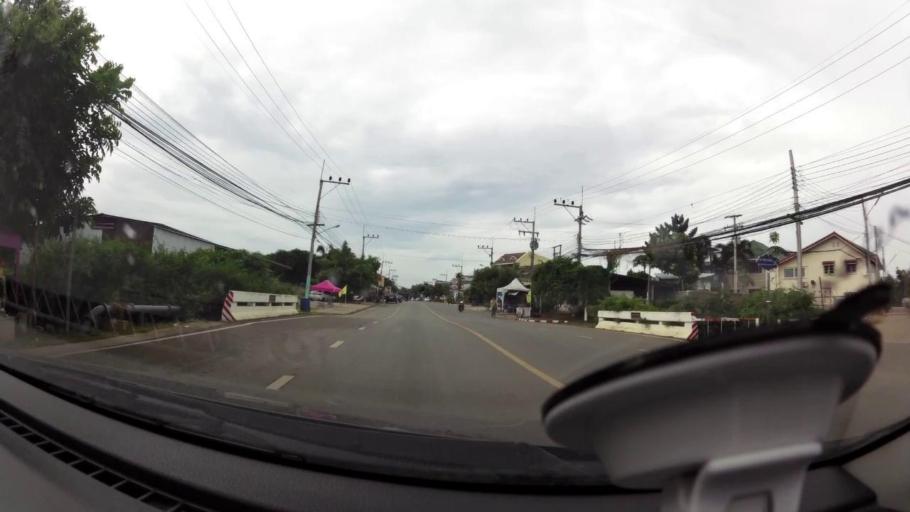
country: TH
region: Prachuap Khiri Khan
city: Pran Buri
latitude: 12.3905
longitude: 99.9862
